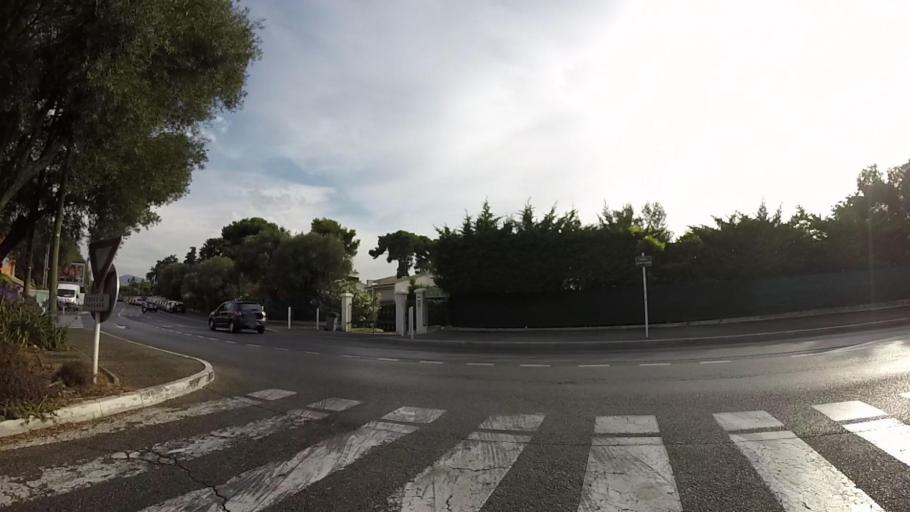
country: FR
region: Provence-Alpes-Cote d'Azur
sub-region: Departement des Alpes-Maritimes
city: Biot
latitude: 43.5949
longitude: 7.1067
